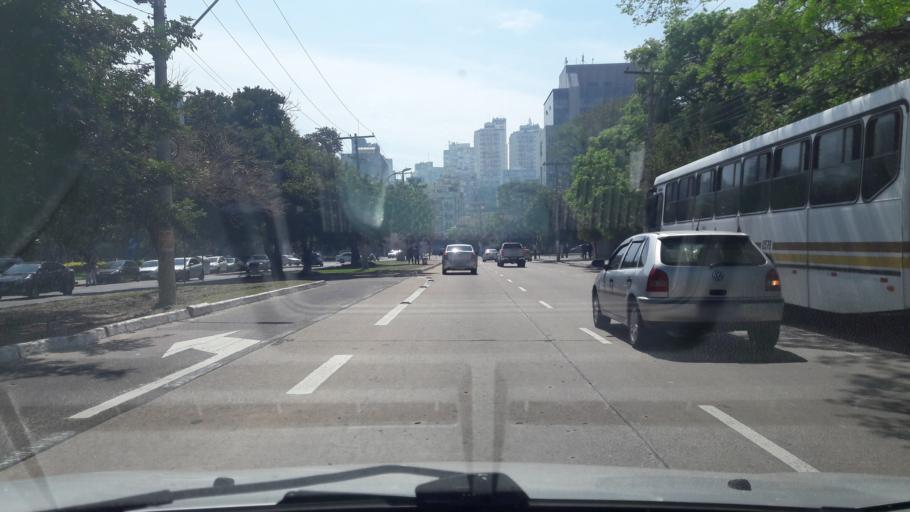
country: BR
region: Rio Grande do Sul
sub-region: Porto Alegre
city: Porto Alegre
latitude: -30.0384
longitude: -51.2328
